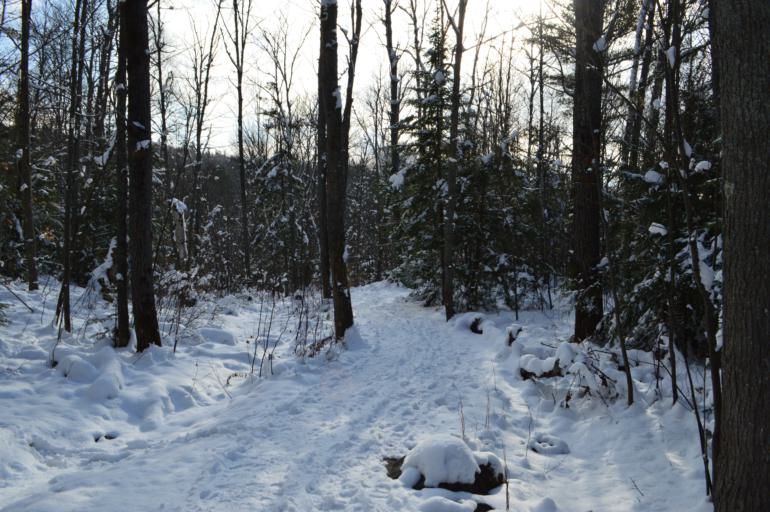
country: CA
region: Ontario
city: Bancroft
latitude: 45.5807
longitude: -78.4080
